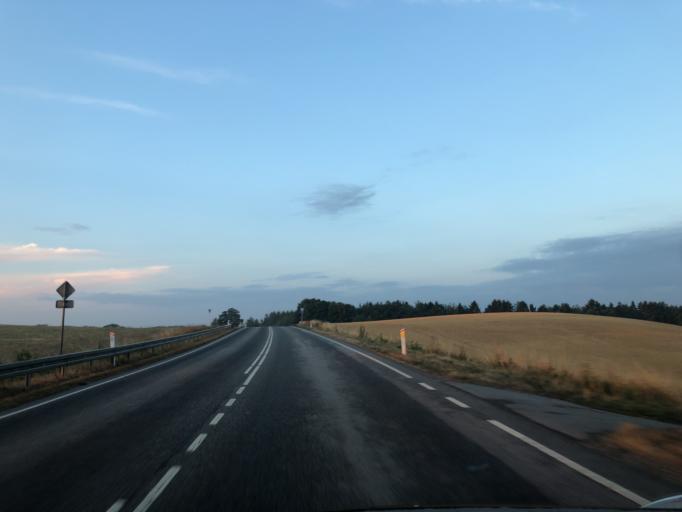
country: DK
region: Zealand
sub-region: Soro Kommune
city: Stenlille
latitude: 55.6017
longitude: 11.6561
